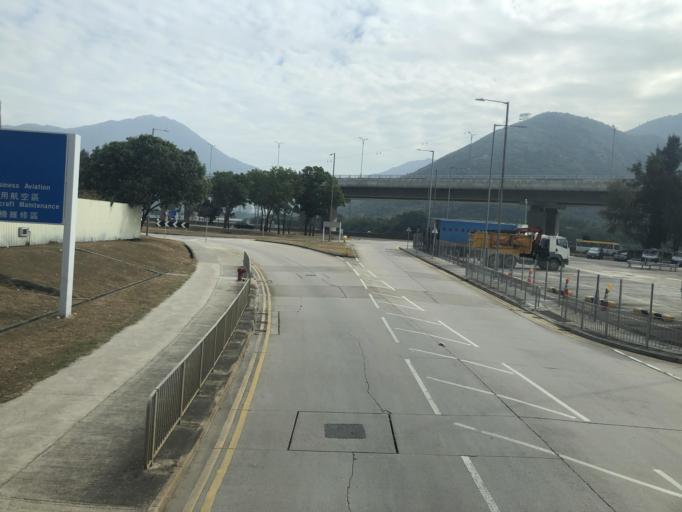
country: HK
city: Tai O
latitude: 22.2952
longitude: 113.9210
